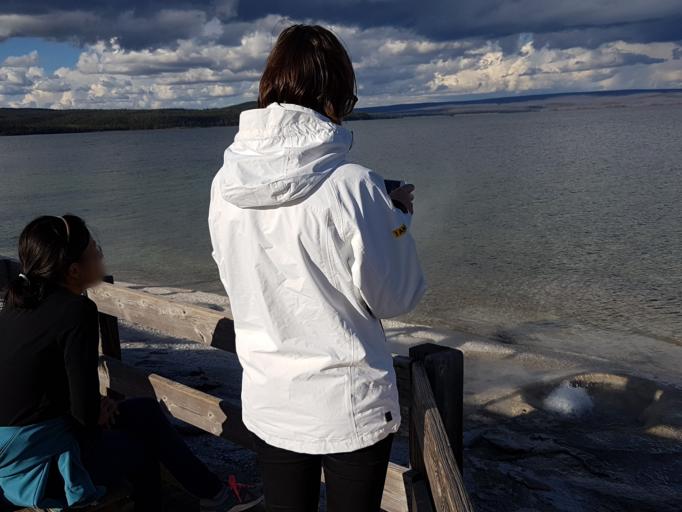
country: US
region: Montana
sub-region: Gallatin County
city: West Yellowstone
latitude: 44.4167
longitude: -110.5700
